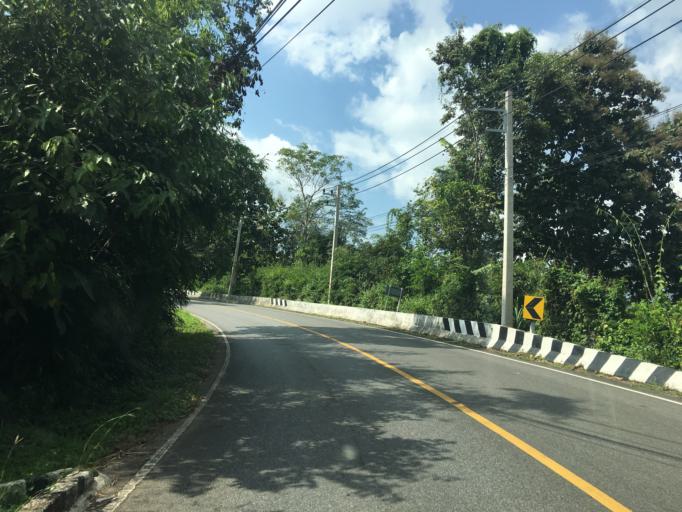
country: TH
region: Nan
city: Nan
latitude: 18.8659
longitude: 100.6201
